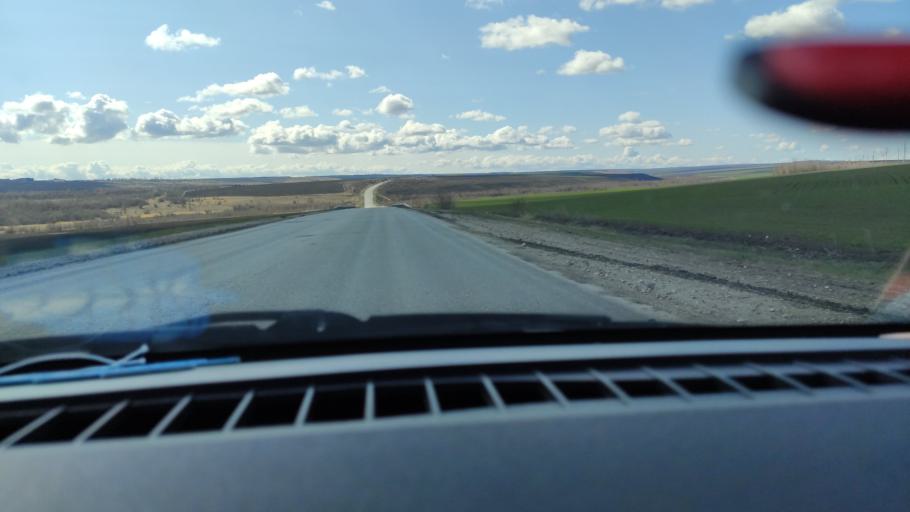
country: RU
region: Samara
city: Varlamovo
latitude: 53.0754
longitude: 48.3541
